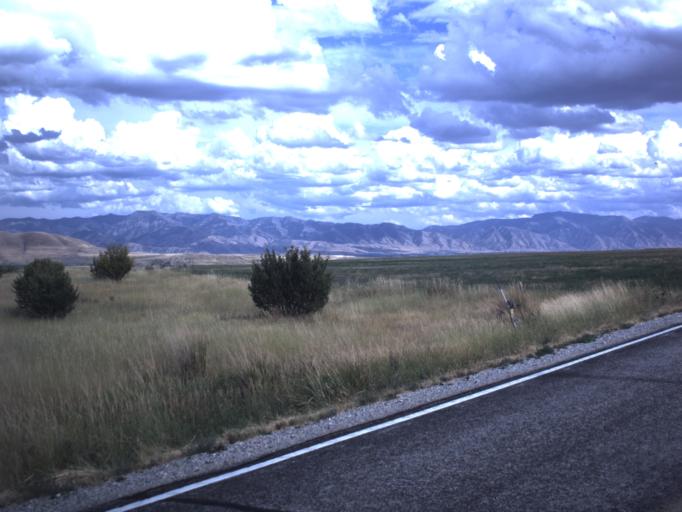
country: US
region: Utah
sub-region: Cache County
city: Benson
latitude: 41.8955
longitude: -112.0433
